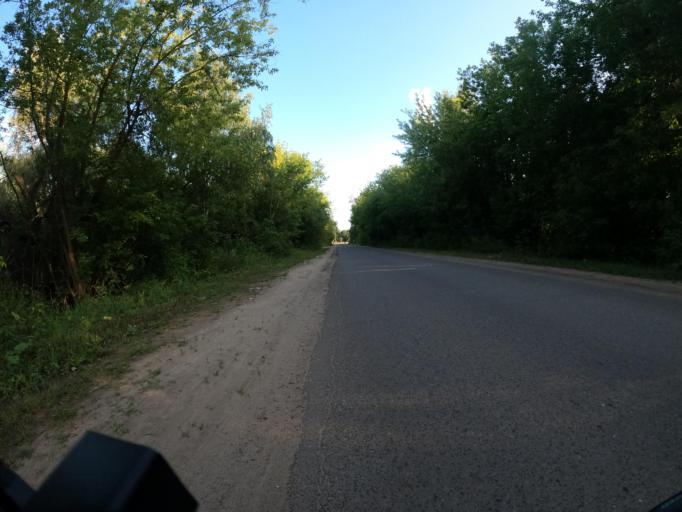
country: RU
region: Moskovskaya
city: Beloozerskiy
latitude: 55.4503
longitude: 38.4889
